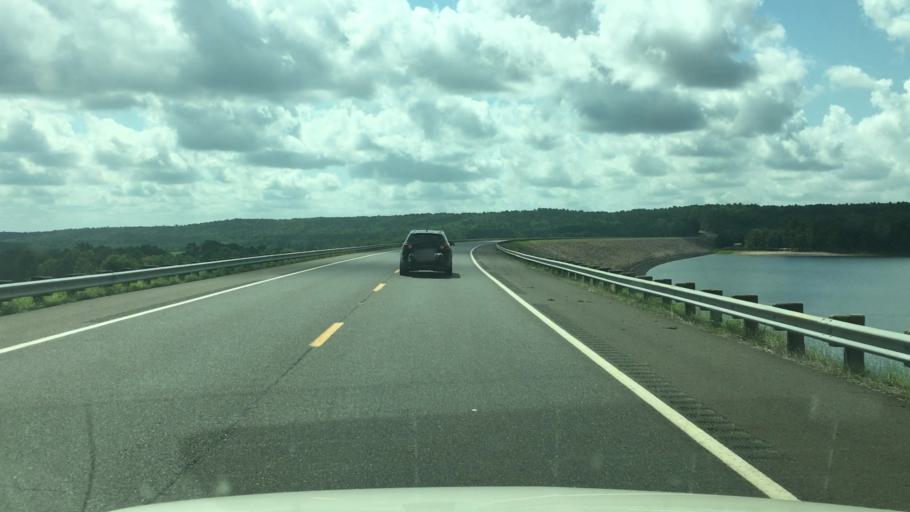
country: US
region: Arkansas
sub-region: Clark County
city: Arkadelphia
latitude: 34.2441
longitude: -93.1073
